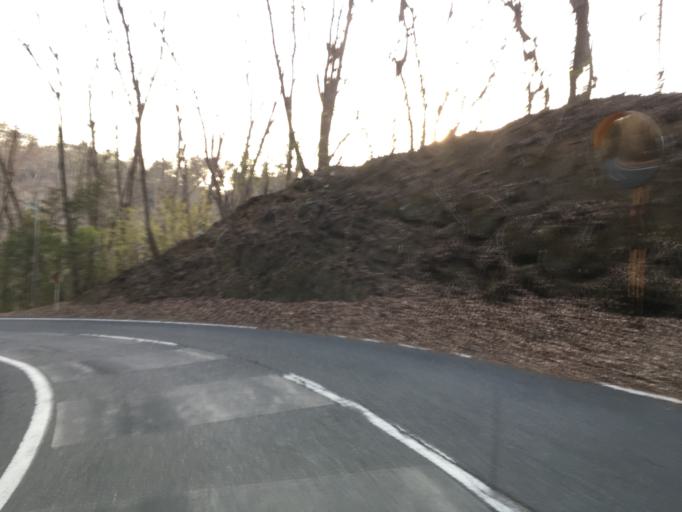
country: JP
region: Ibaraki
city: Daigo
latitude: 36.7970
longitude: 140.3967
